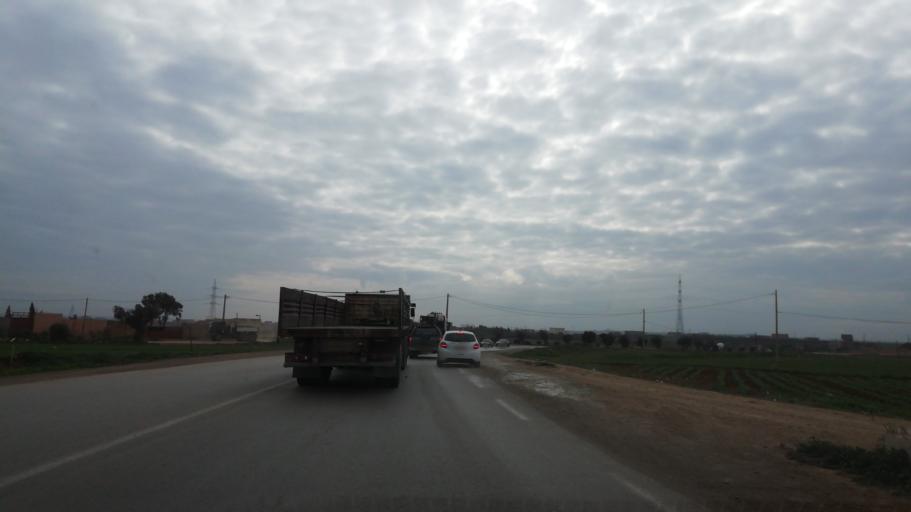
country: DZ
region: Oran
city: Ain el Bya
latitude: 35.7943
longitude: -0.3423
